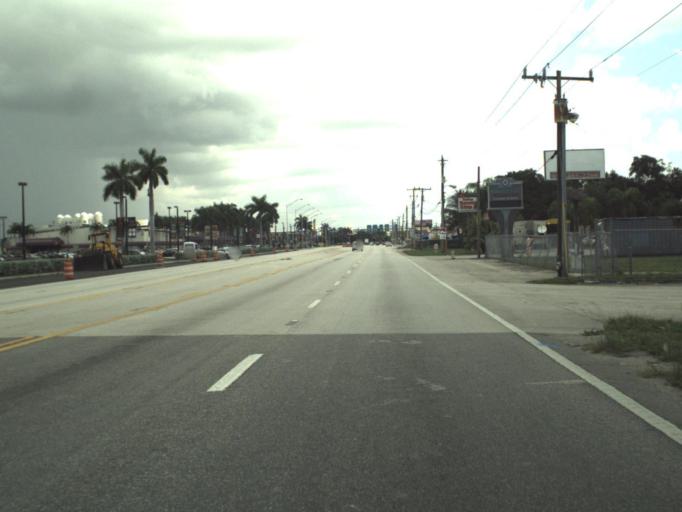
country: US
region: Florida
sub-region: Broward County
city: Davie
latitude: 26.0407
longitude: -80.2086
